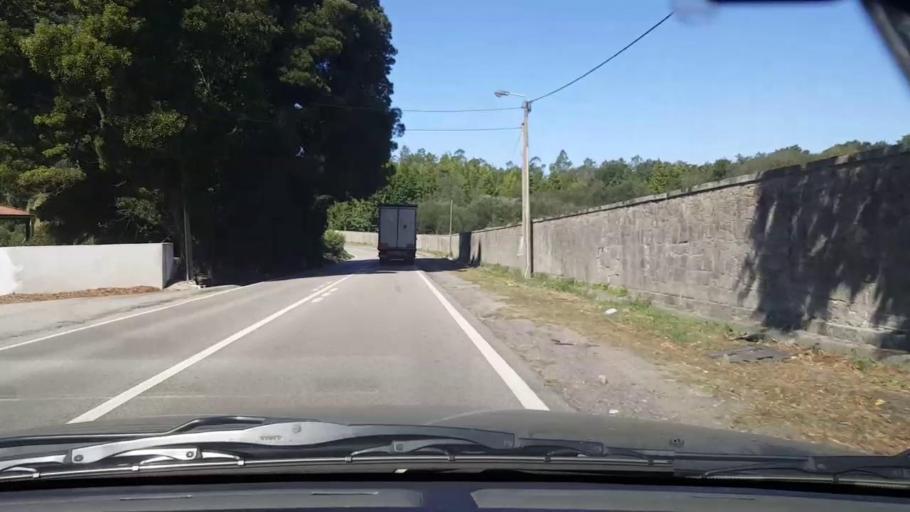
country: PT
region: Porto
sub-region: Vila do Conde
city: Arvore
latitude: 41.3389
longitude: -8.6915
